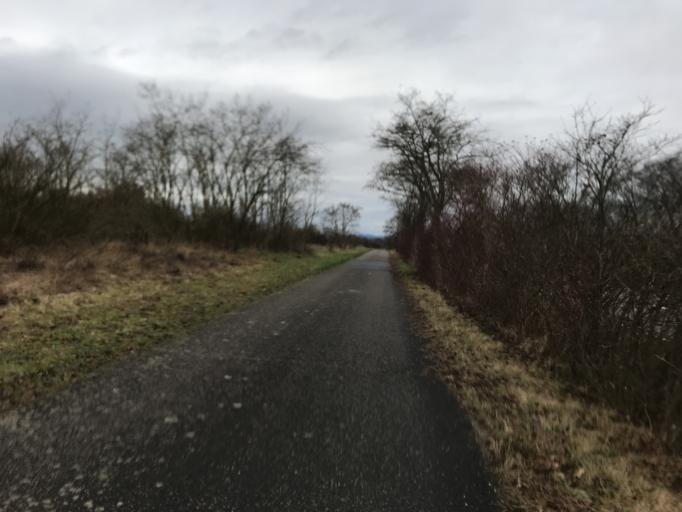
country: DE
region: Rheinland-Pfalz
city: Nieder-Ingelheim
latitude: 49.9926
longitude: 8.0844
